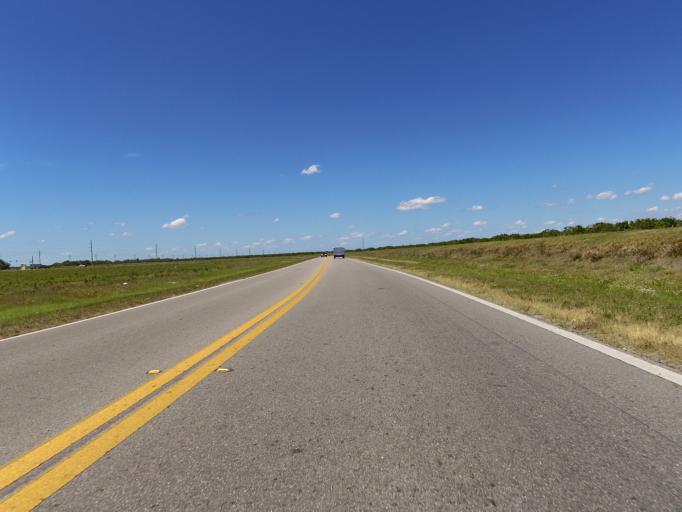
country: US
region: Florida
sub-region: Collier County
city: Immokalee
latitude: 26.3718
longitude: -81.4145
